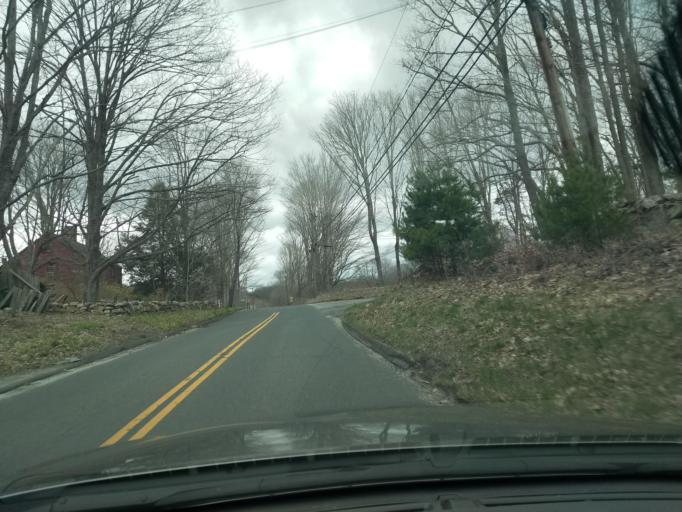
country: US
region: Connecticut
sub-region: Fairfield County
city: Newtown
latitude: 41.3636
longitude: -73.2830
